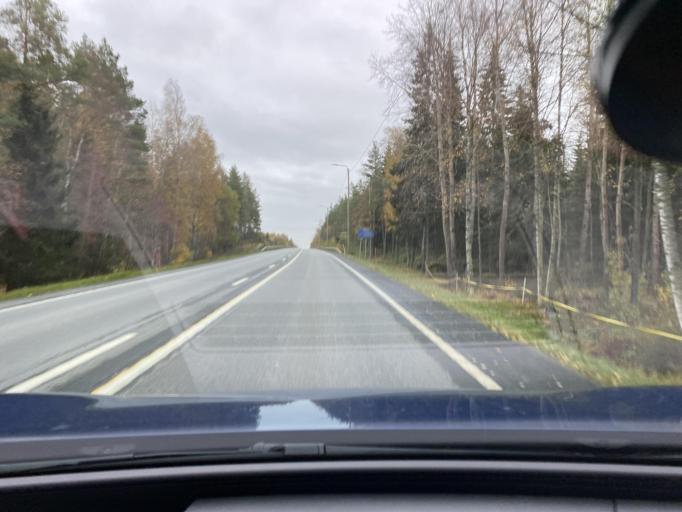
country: FI
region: Varsinais-Suomi
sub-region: Vakka-Suomi
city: Laitila
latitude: 60.9326
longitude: 21.6073
